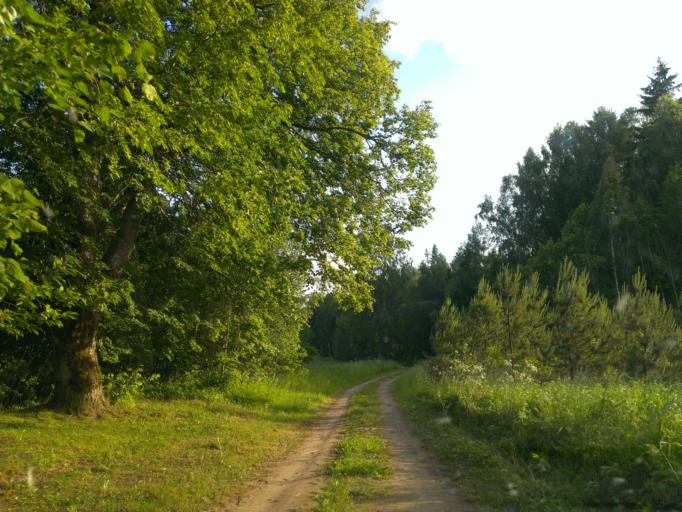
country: LV
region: Skrunda
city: Skrunda
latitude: 56.6913
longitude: 21.8741
